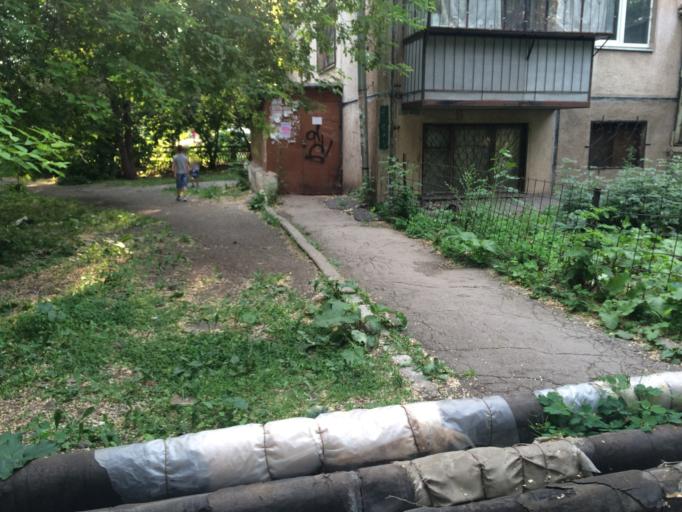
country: RU
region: Chelyabinsk
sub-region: Gorod Magnitogorsk
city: Magnitogorsk
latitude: 53.4036
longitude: 58.9835
